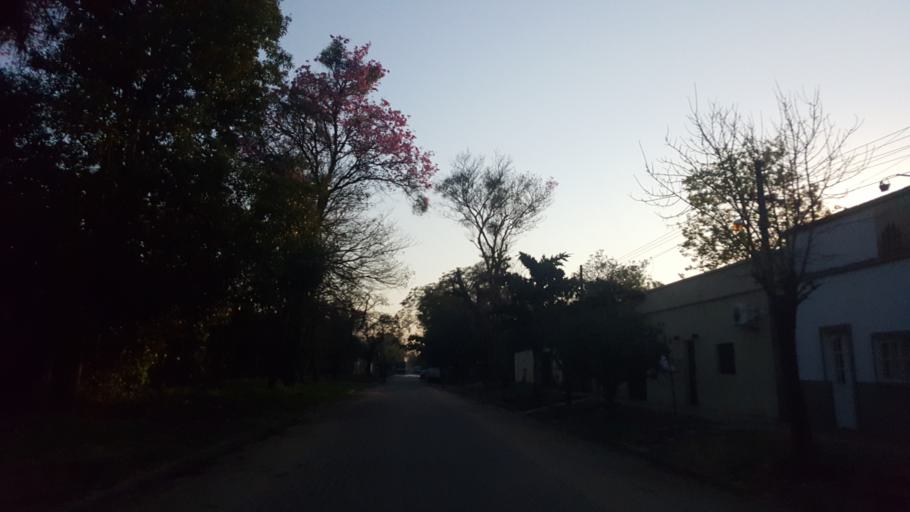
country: AR
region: Corrientes
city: Ituzaingo
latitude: -27.5889
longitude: -56.6876
